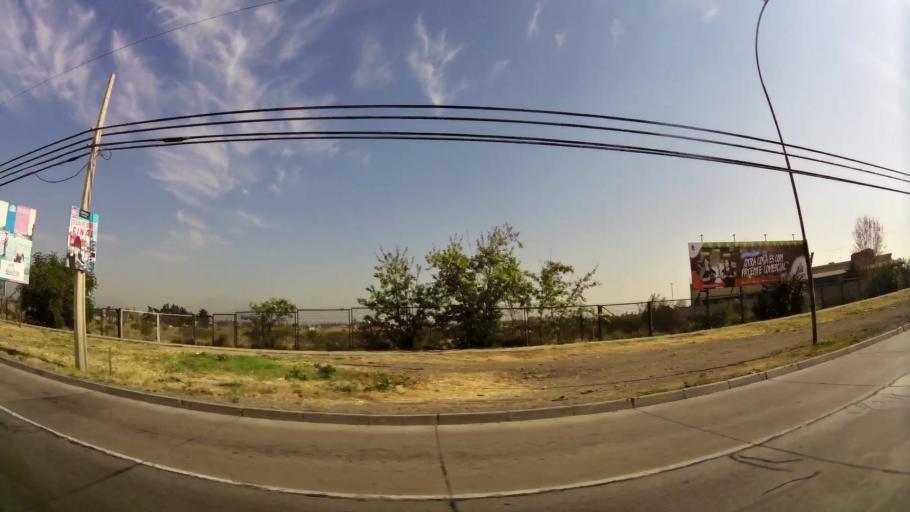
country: CL
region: Santiago Metropolitan
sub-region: Provincia de Santiago
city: Lo Prado
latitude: -33.5174
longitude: -70.7386
